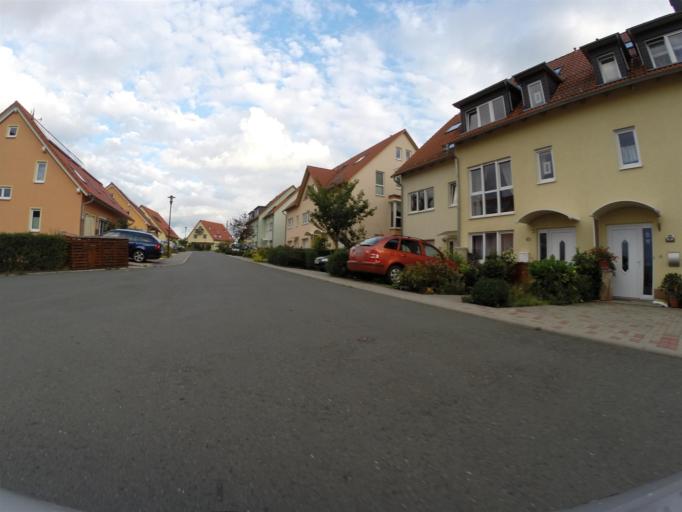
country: DE
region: Thuringia
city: Jena
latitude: 50.9029
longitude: 11.5671
